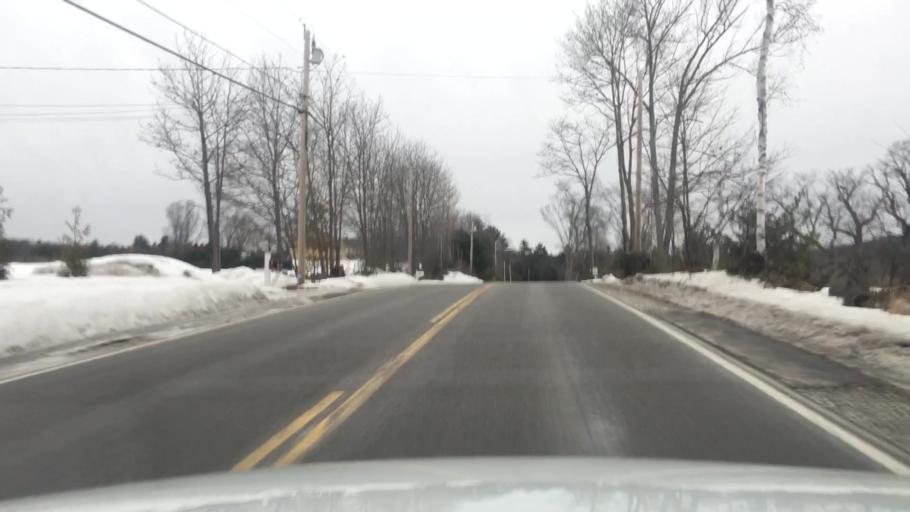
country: US
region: Maine
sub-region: York County
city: Limerick
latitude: 43.7146
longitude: -70.8134
